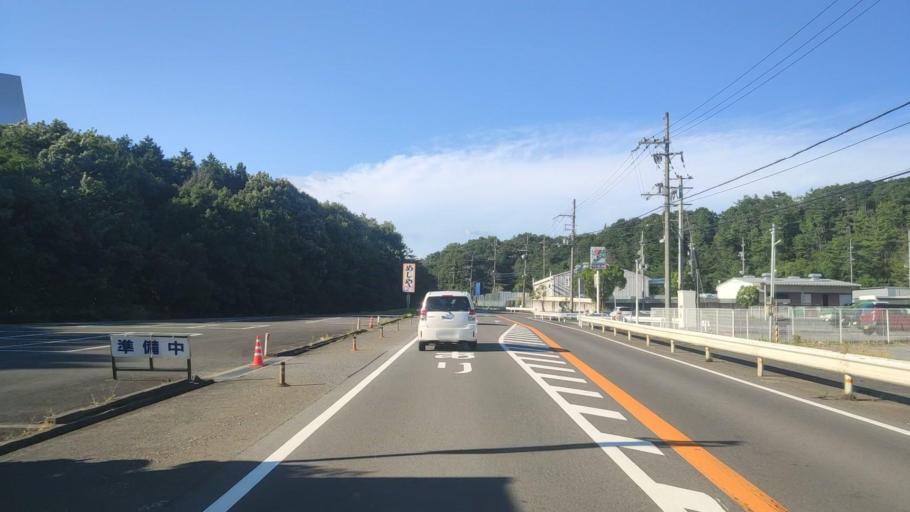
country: JP
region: Shiga Prefecture
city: Hino
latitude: 35.0614
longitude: 136.2470
